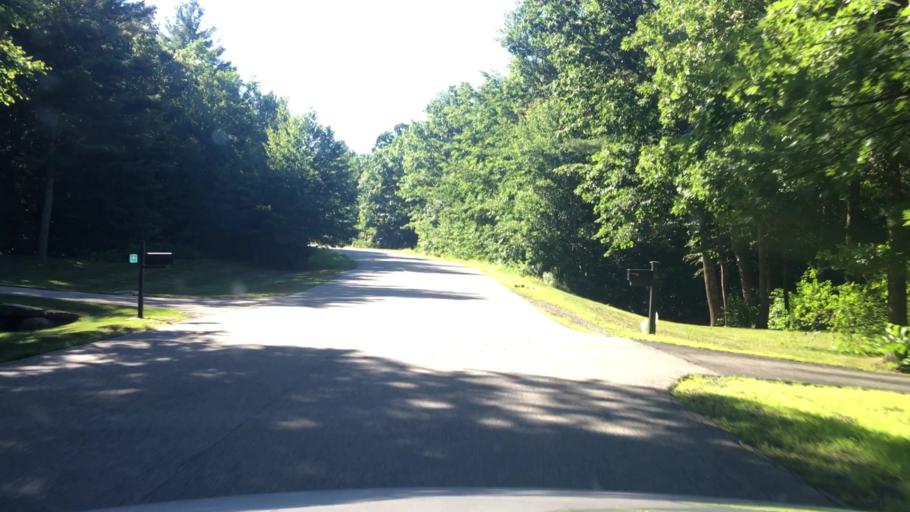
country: US
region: New Hampshire
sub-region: Rockingham County
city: Newmarket
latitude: 43.0355
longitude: -70.9589
